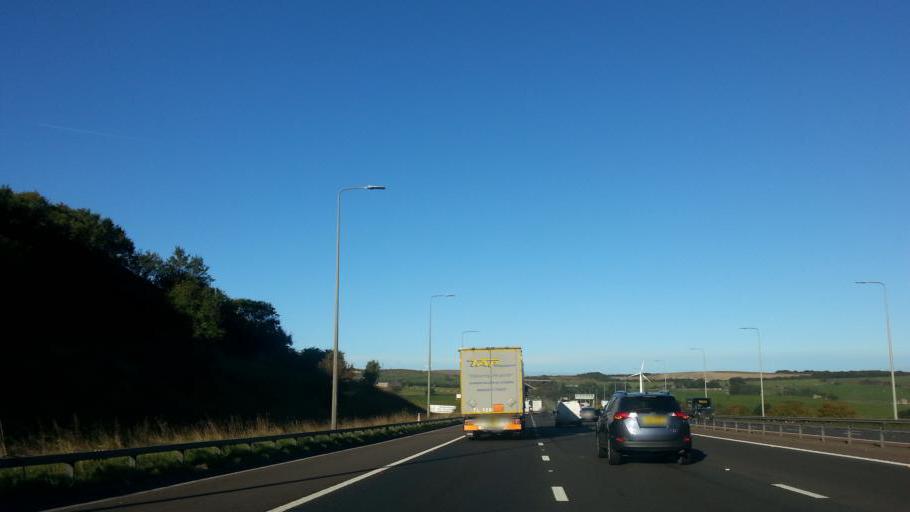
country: GB
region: England
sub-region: Kirklees
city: Marsden
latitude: 53.6445
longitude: -1.9041
